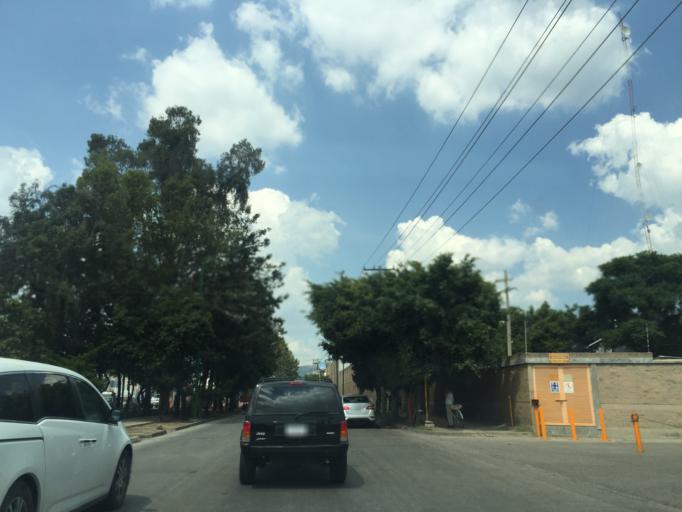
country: MX
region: Guanajuato
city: Leon
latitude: 21.1589
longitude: -101.6665
